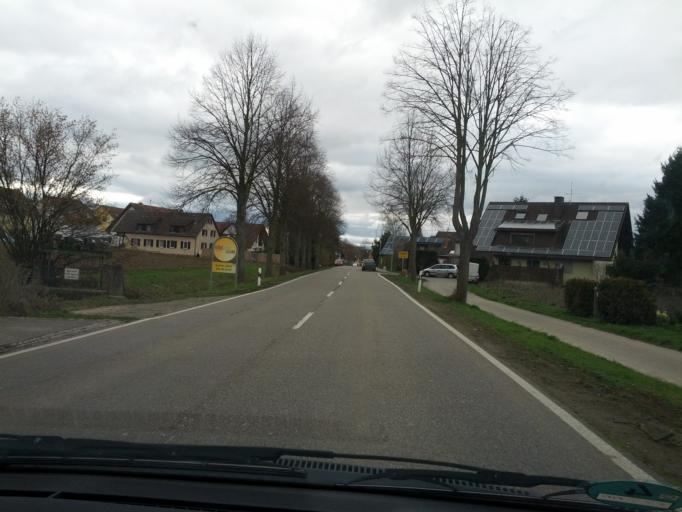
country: DE
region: Baden-Wuerttemberg
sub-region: Freiburg Region
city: Eschbach
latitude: 47.8894
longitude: 7.6632
